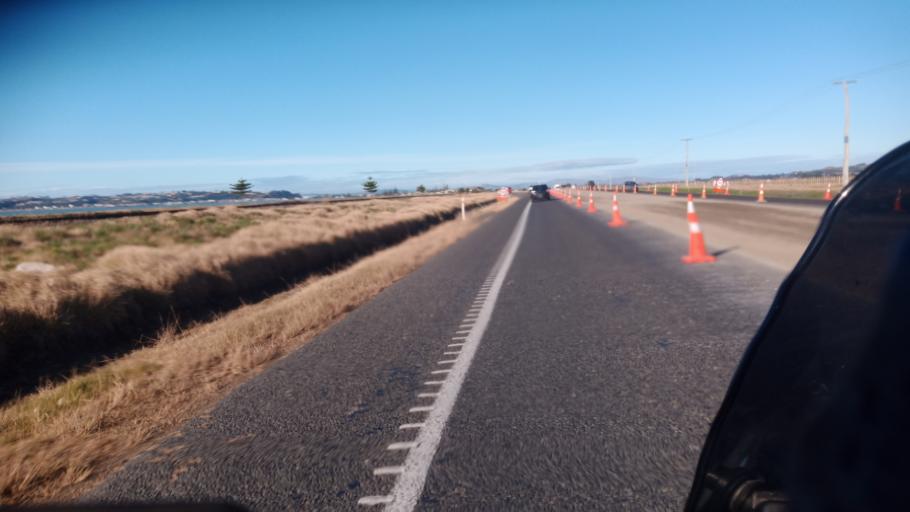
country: NZ
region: Hawke's Bay
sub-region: Napier City
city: Napier
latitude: -39.4501
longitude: 176.8715
